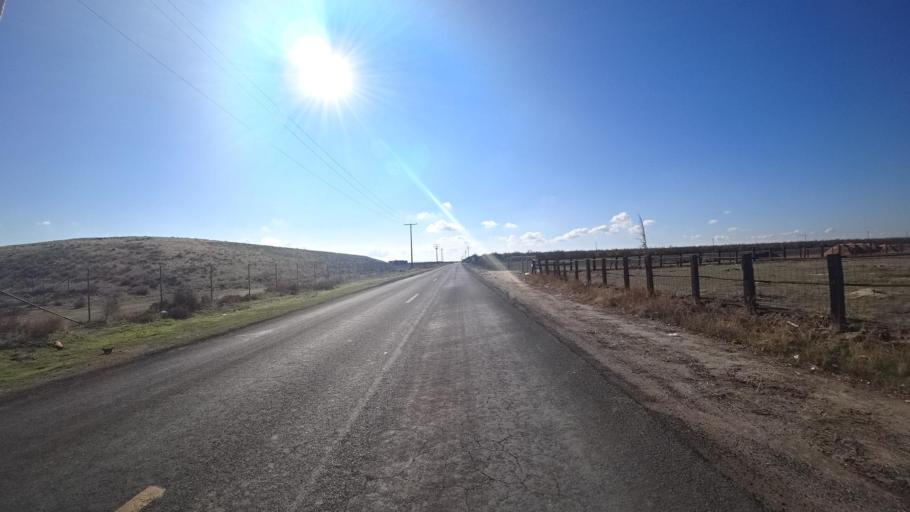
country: US
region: California
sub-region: Kern County
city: Delano
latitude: 35.7418
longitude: -119.2584
